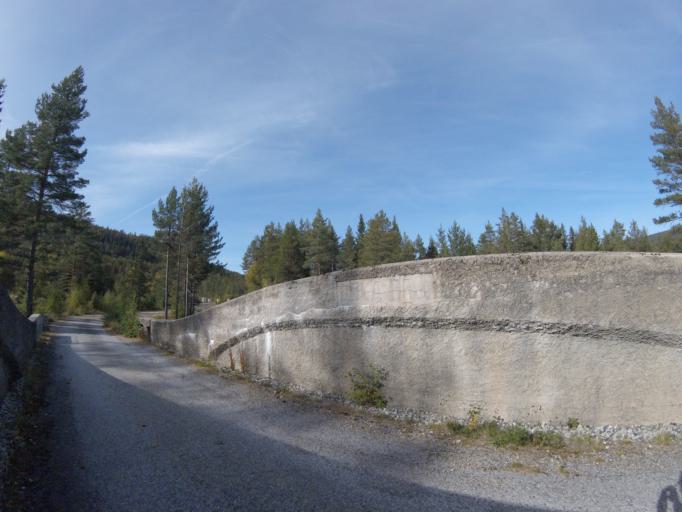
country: NO
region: Telemark
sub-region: Notodden
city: Notodden
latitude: 59.7109
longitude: 9.4048
